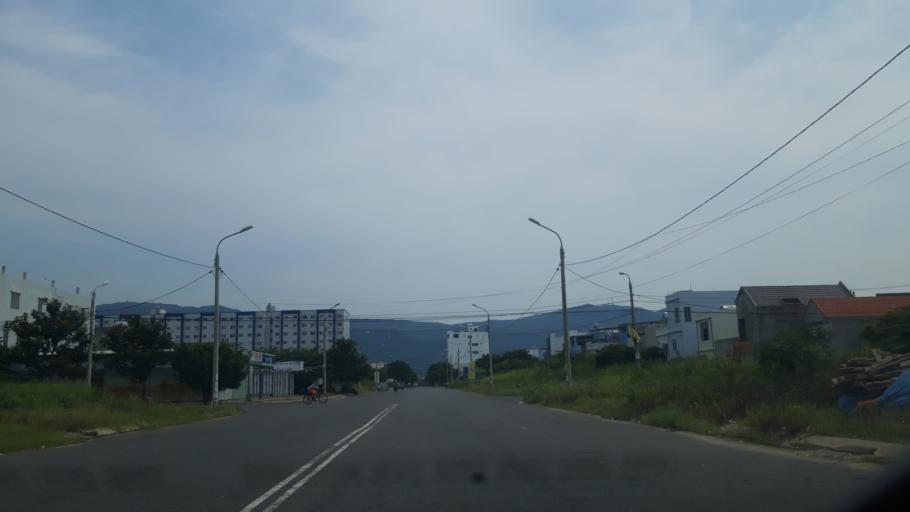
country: VN
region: Da Nang
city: Da Nang
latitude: 16.0902
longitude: 108.2278
